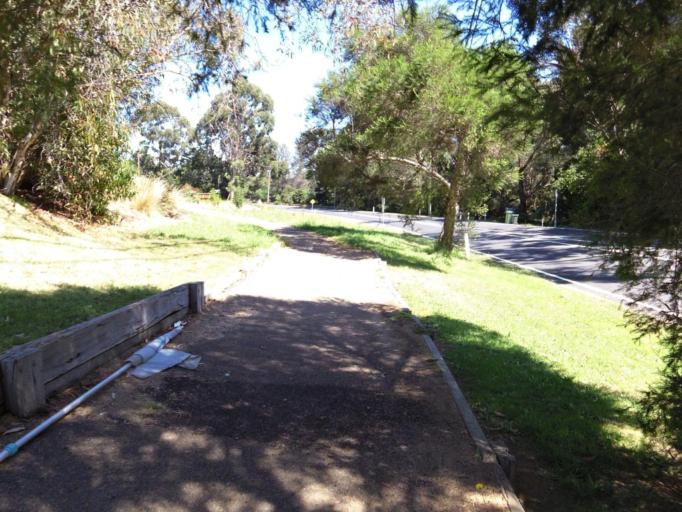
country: AU
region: Victoria
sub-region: Mornington Peninsula
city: Merricks
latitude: -38.3805
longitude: 145.0249
